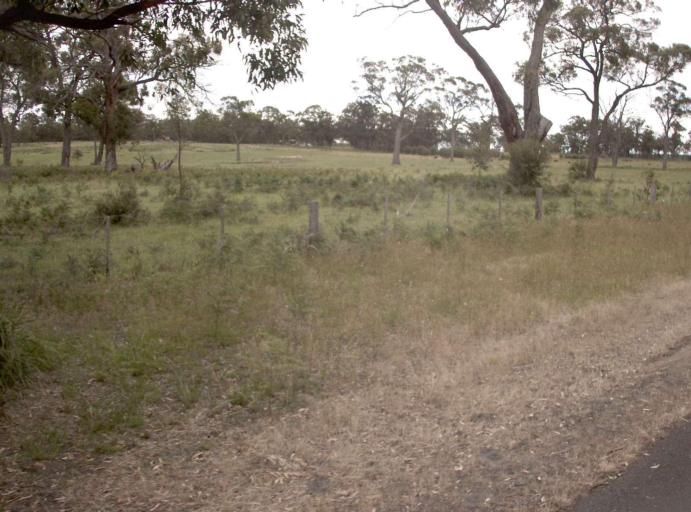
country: AU
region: Victoria
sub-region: Wellington
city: Sale
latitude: -38.2340
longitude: 147.0544
